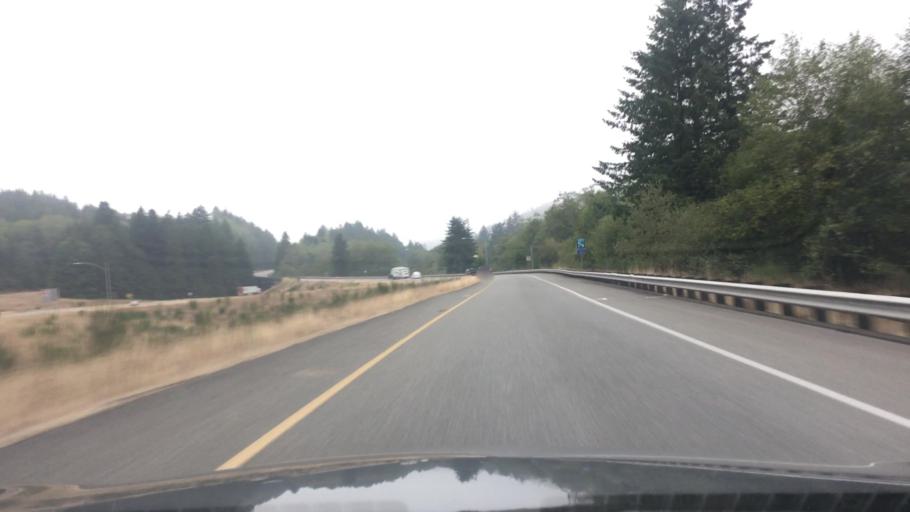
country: US
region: Washington
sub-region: Jefferson County
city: Port Hadlock-Irondale
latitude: 47.9558
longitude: -122.8833
